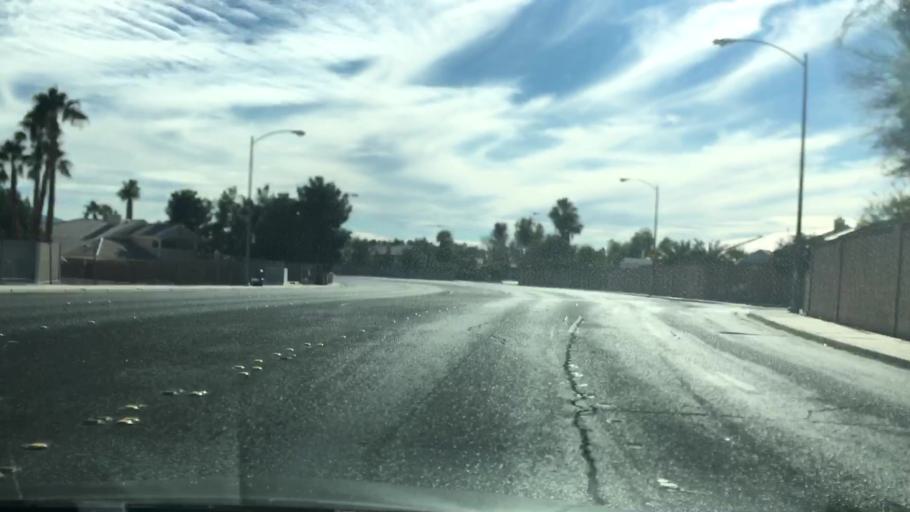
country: US
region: Nevada
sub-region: Clark County
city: Paradise
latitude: 36.0479
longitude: -115.1408
